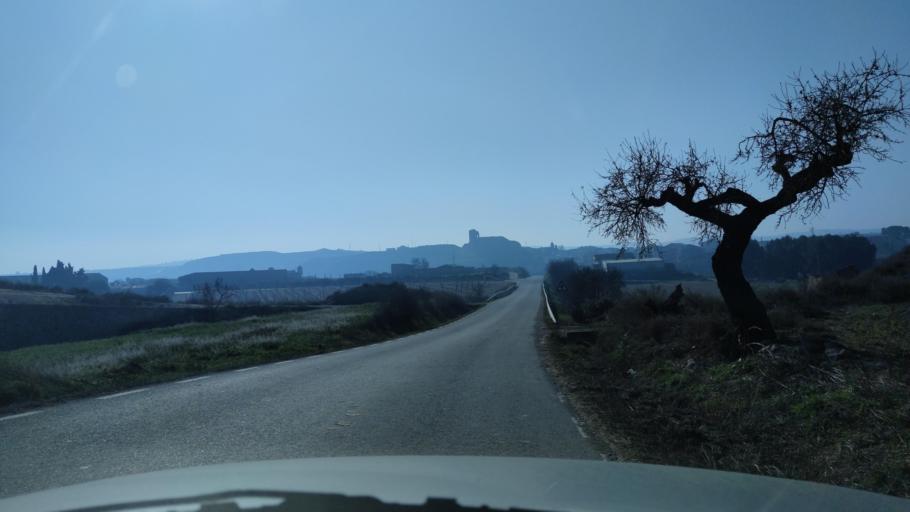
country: ES
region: Catalonia
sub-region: Provincia de Lleida
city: Torrebesses
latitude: 41.4637
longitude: 0.5655
